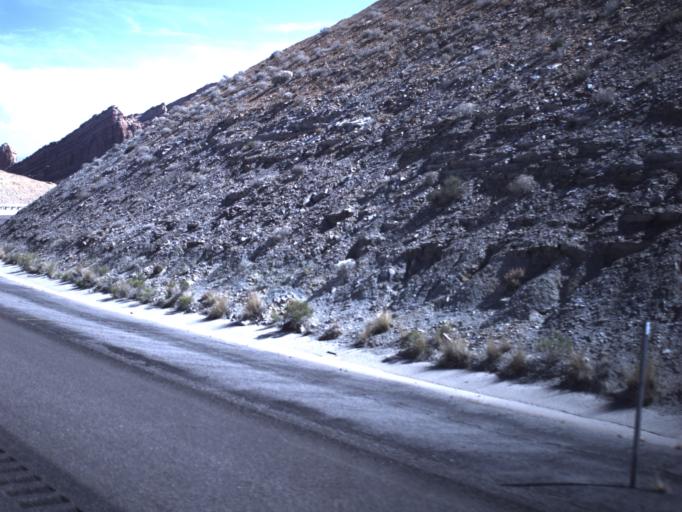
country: US
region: Utah
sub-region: Carbon County
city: East Carbon City
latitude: 38.9372
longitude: -110.4652
